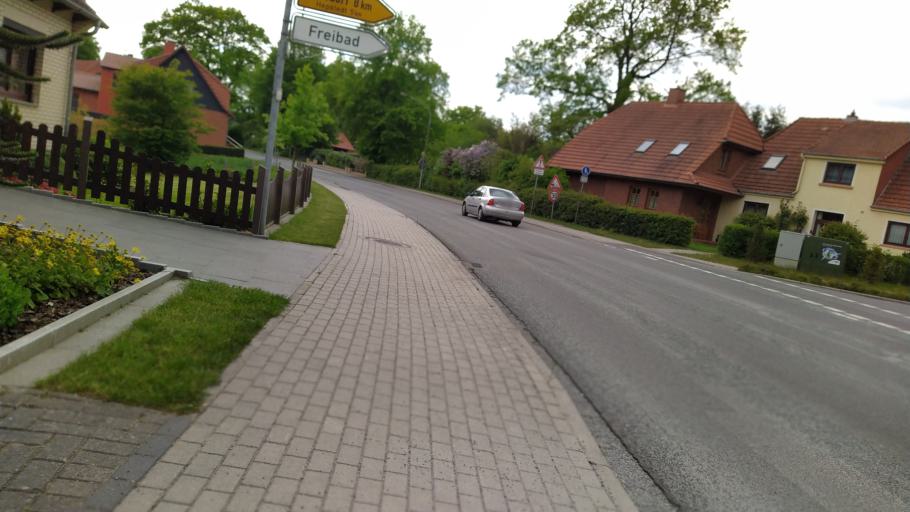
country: DE
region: Lower Saxony
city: Kirchtimke
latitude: 53.2509
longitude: 9.1509
